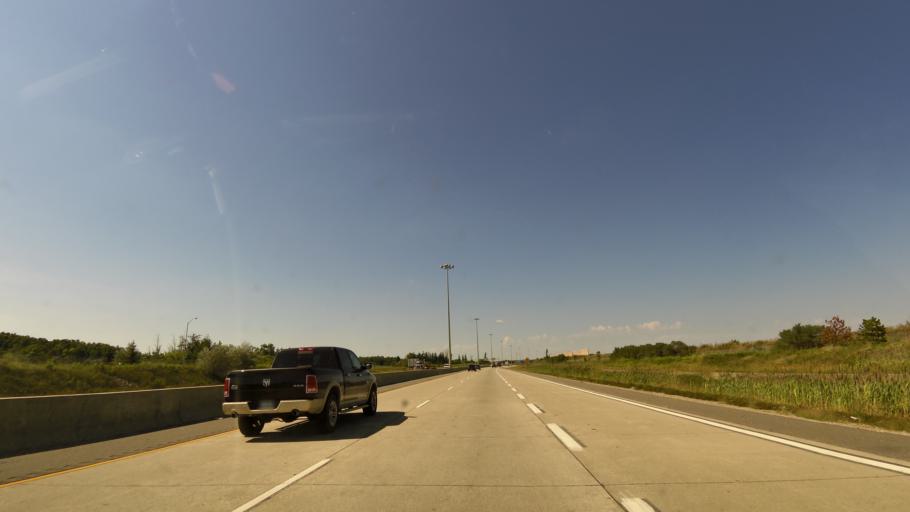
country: CA
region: Ontario
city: Brampton
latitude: 43.7400
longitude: -79.7802
